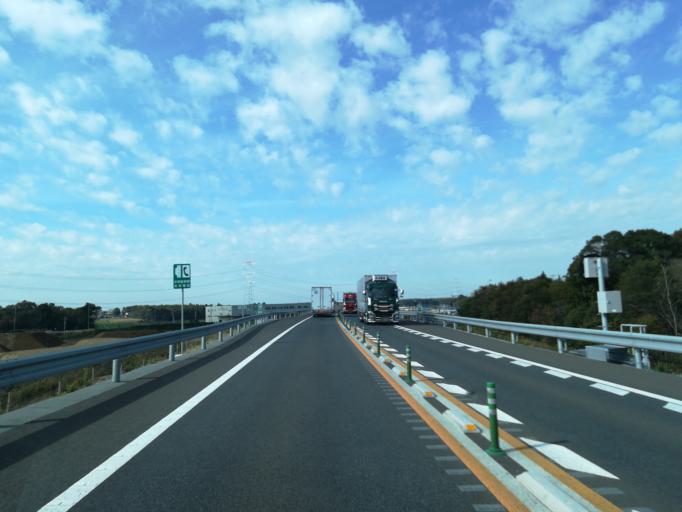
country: JP
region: Ibaraki
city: Mitsukaido
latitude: 36.0565
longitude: 140.0499
